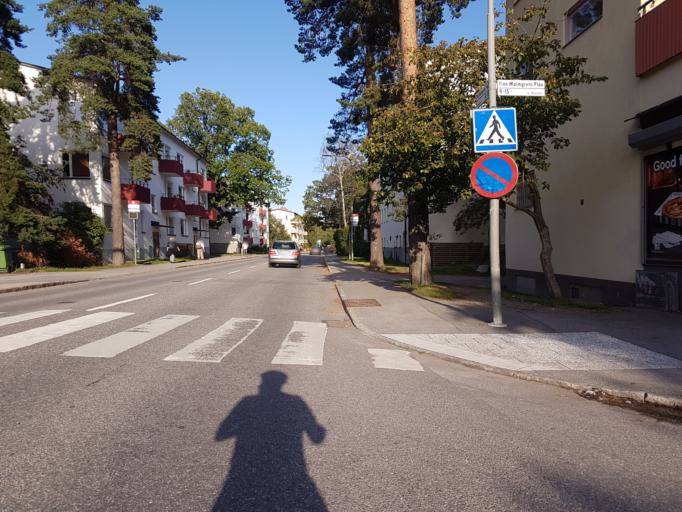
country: SE
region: Stockholm
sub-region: Stockholms Kommun
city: OEstermalm
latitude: 59.2954
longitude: 18.1025
